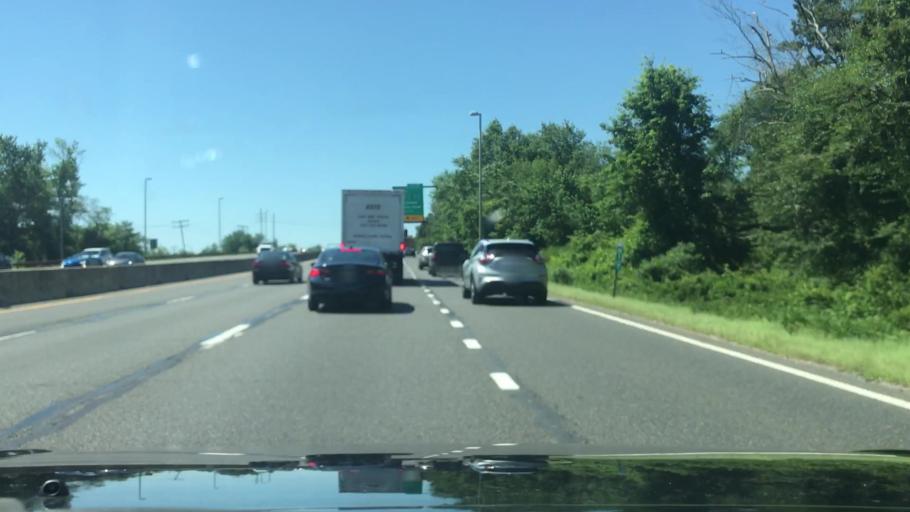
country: US
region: New Jersey
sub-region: Ocean County
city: Toms River
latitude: 39.9551
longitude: -74.2067
